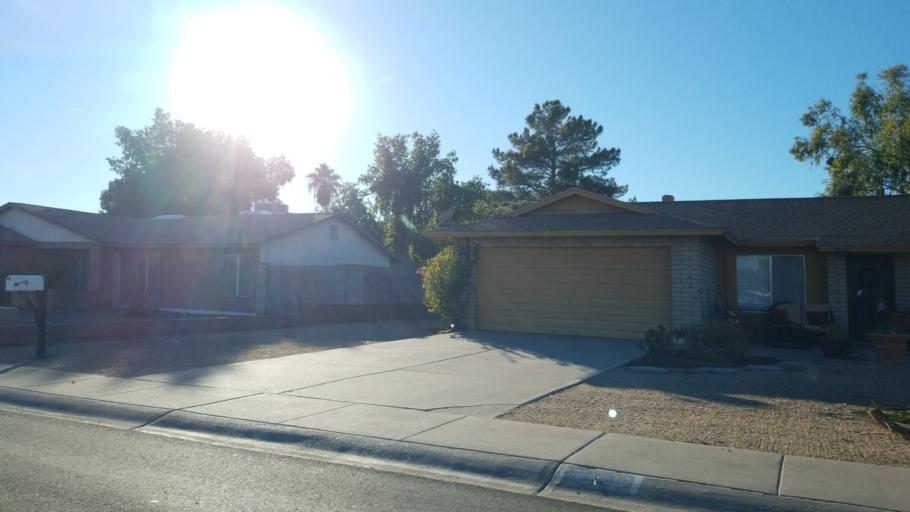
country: US
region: Arizona
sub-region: Maricopa County
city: Paradise Valley
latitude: 33.6002
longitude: -111.9742
